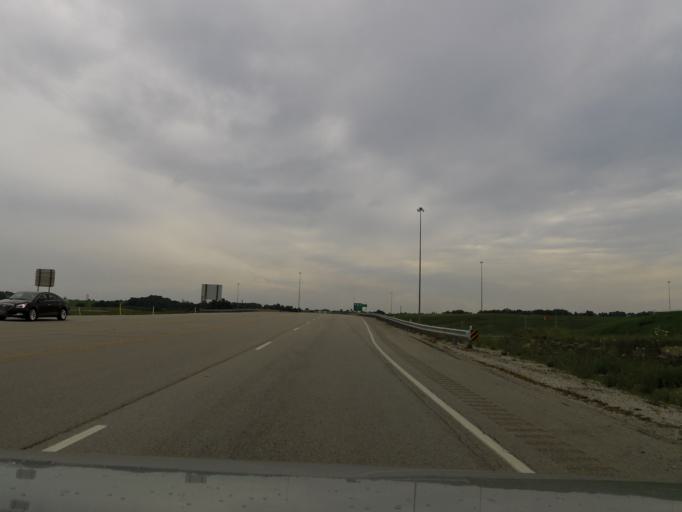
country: US
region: Ohio
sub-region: Brown County
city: Aberdeen
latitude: 38.6449
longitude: -83.8316
